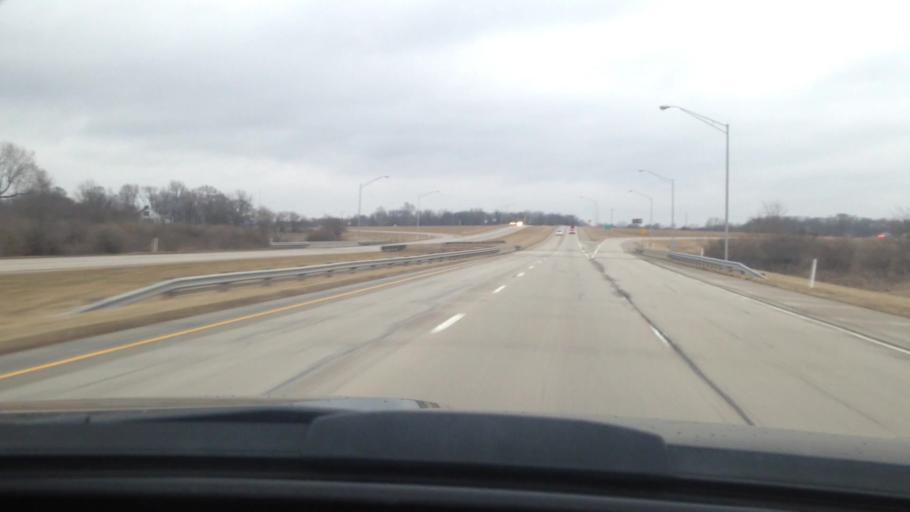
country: US
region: Indiana
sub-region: Delaware County
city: Muncie
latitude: 40.1842
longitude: -85.3365
